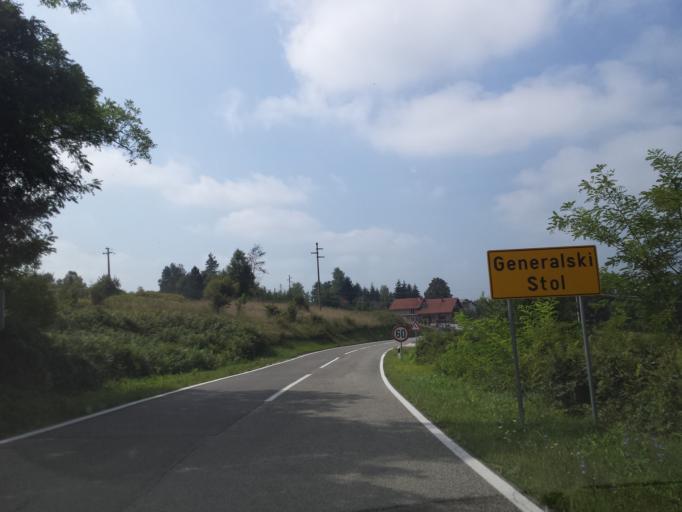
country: HR
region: Karlovacka
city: Ostarije
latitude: 45.3526
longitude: 15.3807
